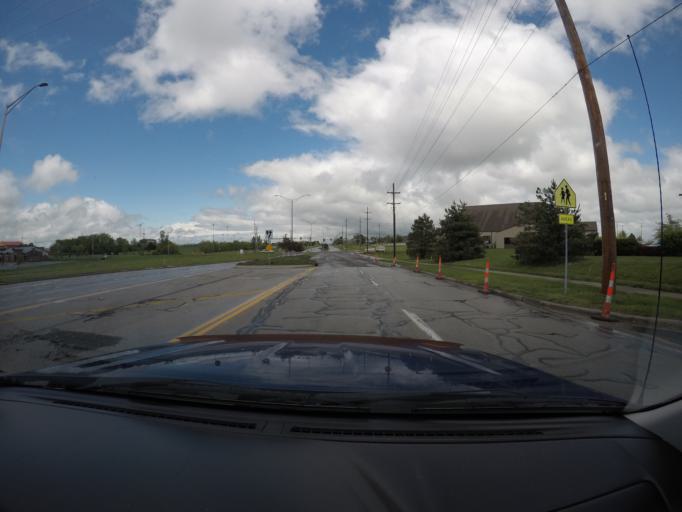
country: US
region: Kansas
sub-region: Johnson County
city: Olathe
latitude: 38.9260
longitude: -94.8345
